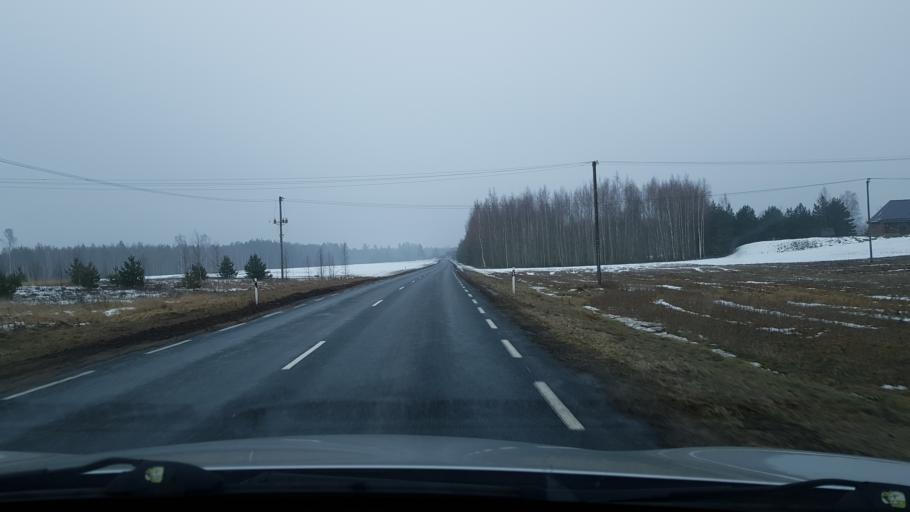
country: EE
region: Valgamaa
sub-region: Torva linn
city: Torva
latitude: 58.1349
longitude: 25.9902
